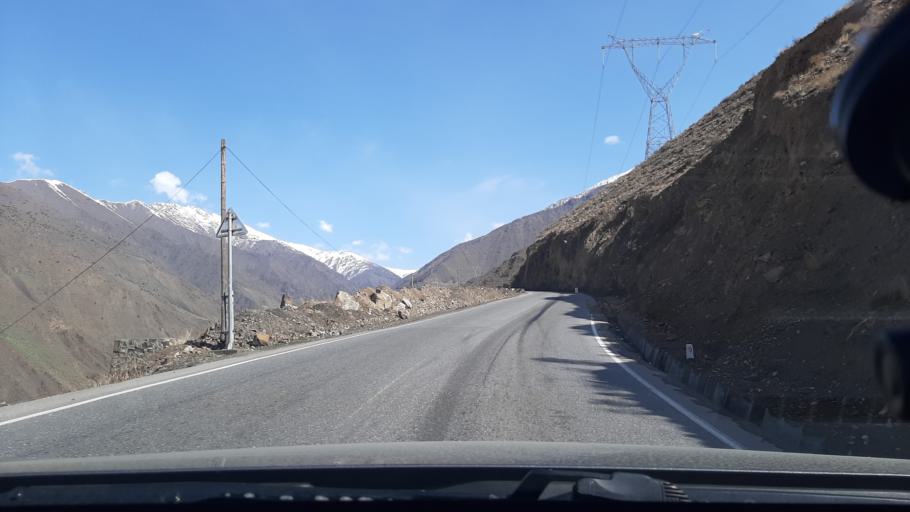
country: TJ
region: Viloyati Sughd
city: Ayni
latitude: 39.4368
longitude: 68.5477
